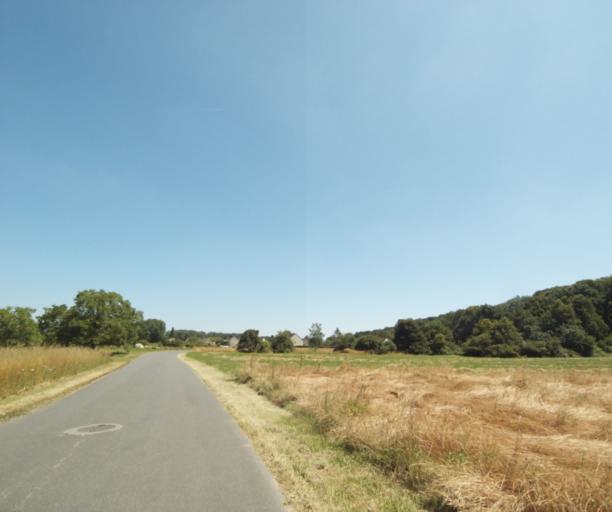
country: FR
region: Ile-de-France
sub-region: Departement de Seine-et-Marne
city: Noisy-sur-Ecole
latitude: 48.3736
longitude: 2.4885
